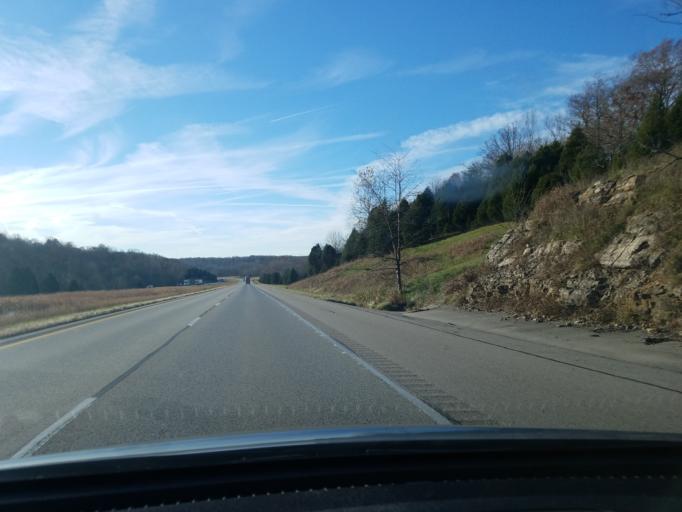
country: US
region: Indiana
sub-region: Harrison County
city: Corydon
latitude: 38.2543
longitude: -86.2966
